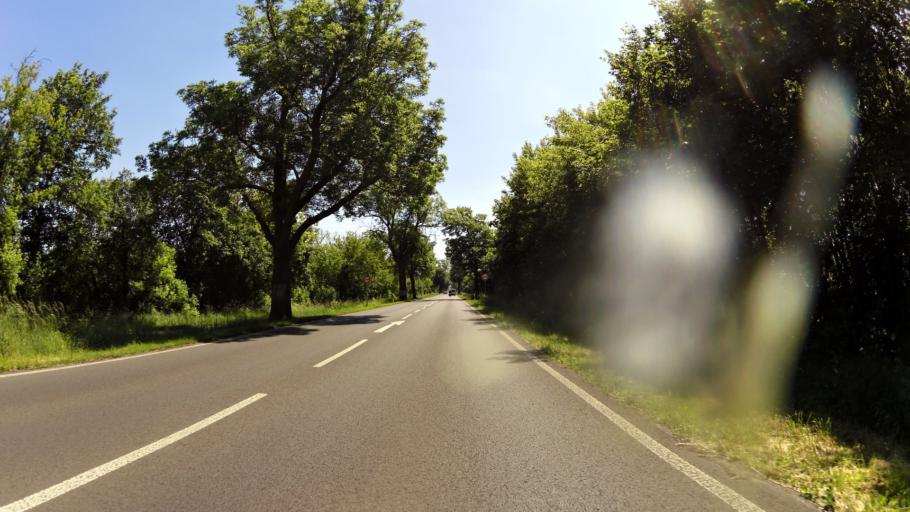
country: DE
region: Brandenburg
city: Lebus
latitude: 52.3828
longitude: 14.5191
